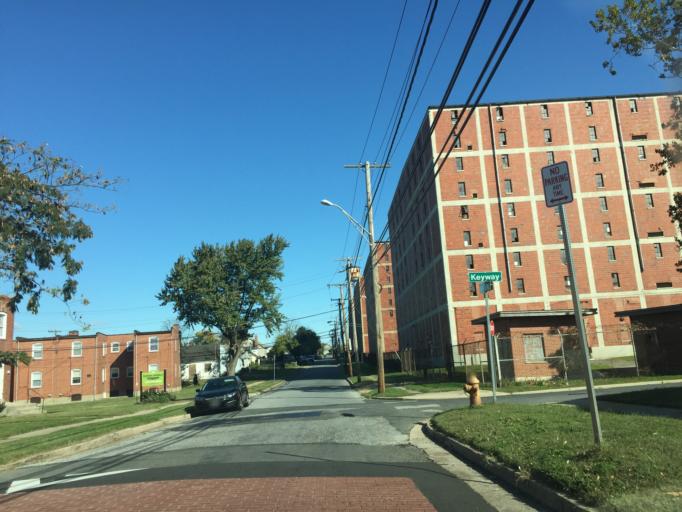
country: US
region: Maryland
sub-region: Baltimore County
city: Dundalk
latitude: 39.2660
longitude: -76.5267
